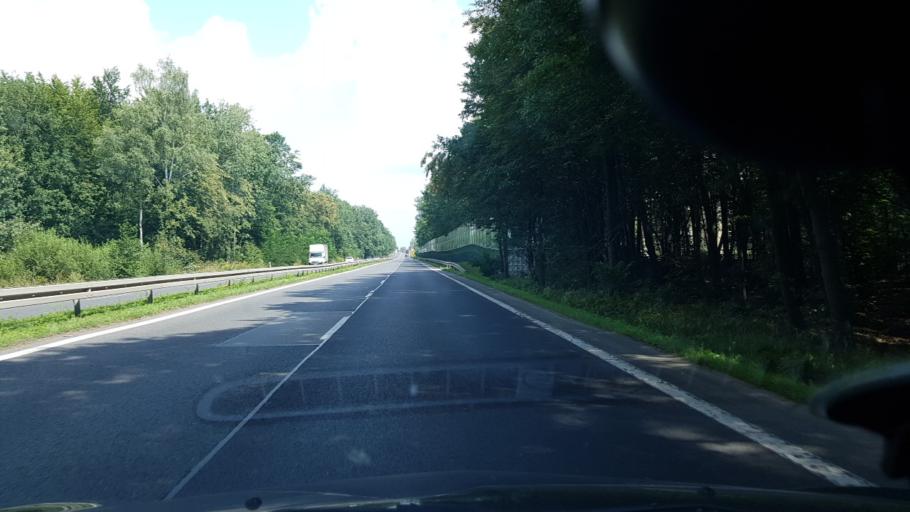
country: PL
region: Silesian Voivodeship
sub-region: Powiat mikolowski
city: Mikolow
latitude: 50.2053
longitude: 18.9536
